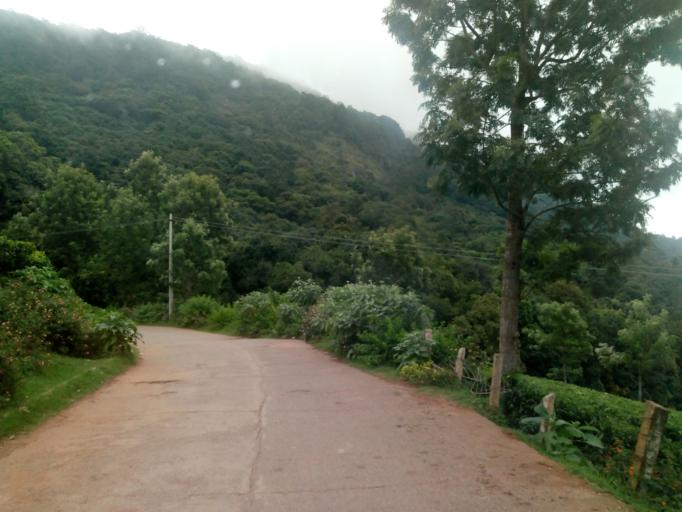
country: IN
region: Tamil Nadu
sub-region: Nilgiri
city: Wellington
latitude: 11.3487
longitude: 76.8164
